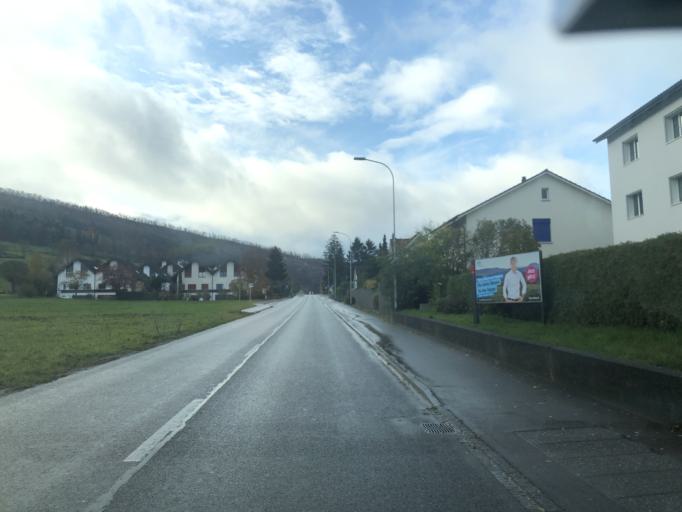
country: CH
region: Aargau
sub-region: Bezirk Baden
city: Unterehrendingen
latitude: 47.4885
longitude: 8.3364
